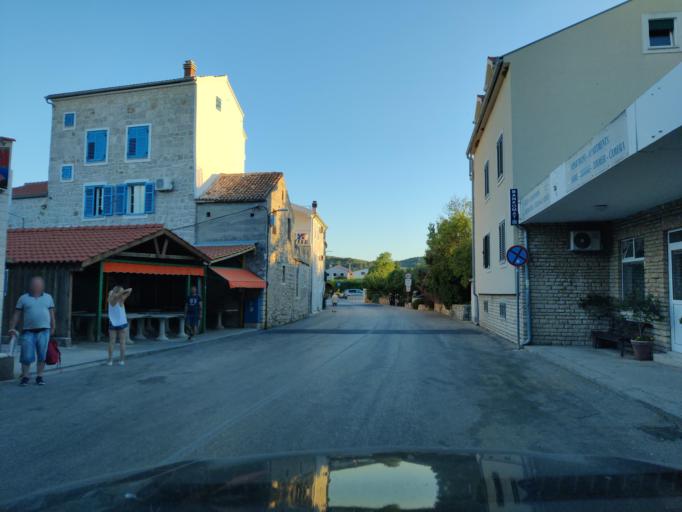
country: HR
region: Sibensko-Kniniska
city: Murter
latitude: 43.8230
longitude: 15.6037
